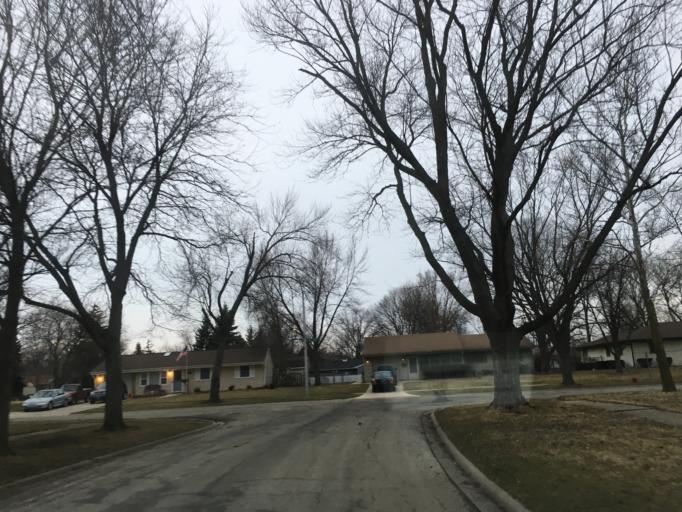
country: US
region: Illinois
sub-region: DuPage County
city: Hanover Park
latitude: 42.0243
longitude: -88.1208
